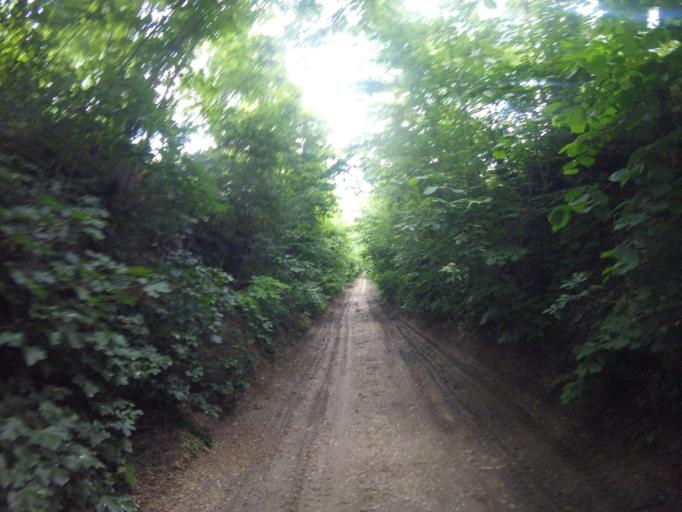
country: HU
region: Zala
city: Zalaszentgrot
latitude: 46.8858
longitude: 17.0346
